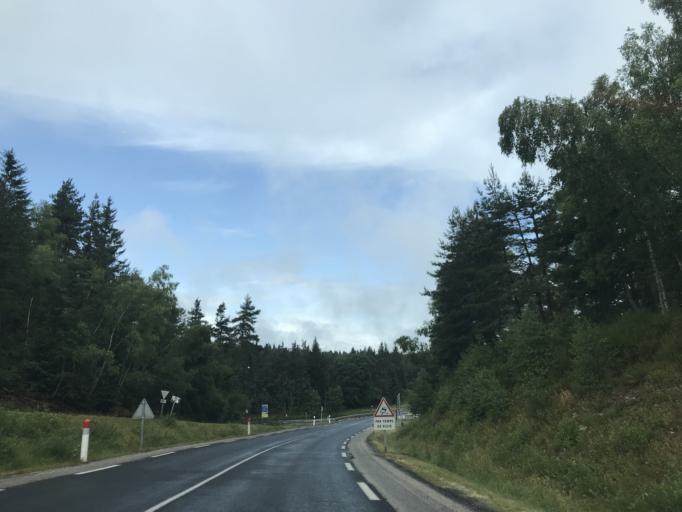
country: FR
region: Auvergne
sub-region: Departement de la Haute-Loire
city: Fontannes
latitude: 45.3370
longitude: 3.7085
